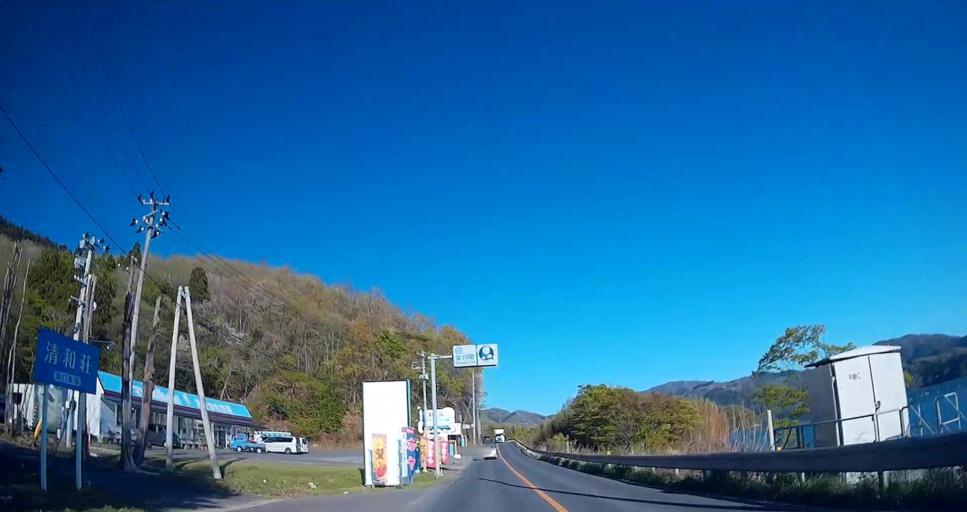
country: JP
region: Miyagi
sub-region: Oshika Gun
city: Onagawa Cho
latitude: 38.4369
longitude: 141.4008
